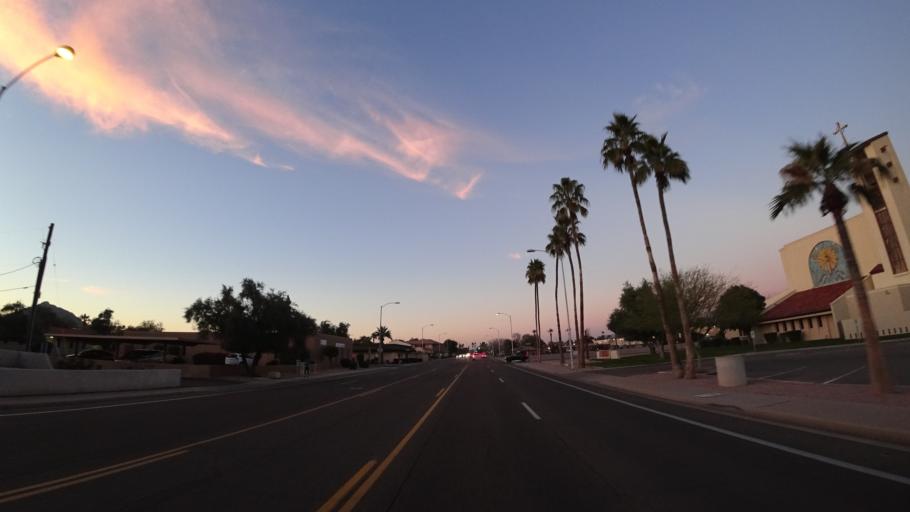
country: US
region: Arizona
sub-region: Maricopa County
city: Scottsdale
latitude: 33.4924
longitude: -111.9175
